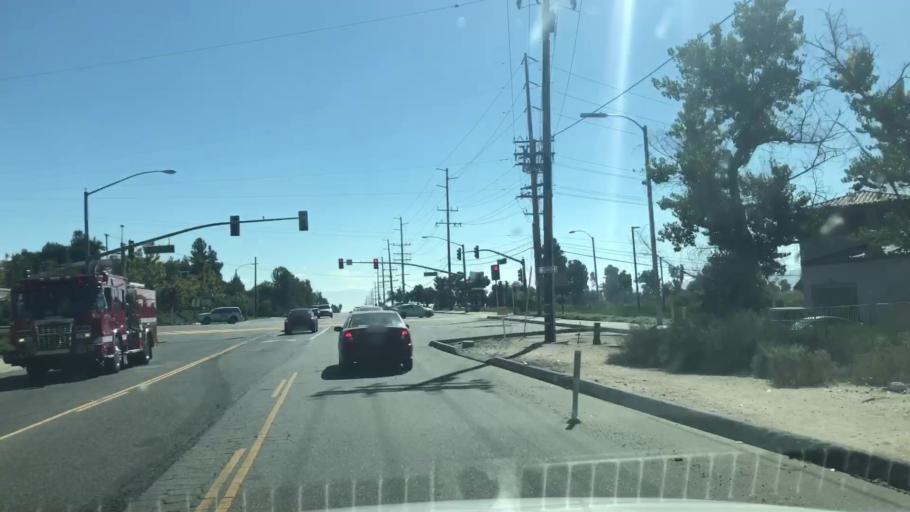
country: US
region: California
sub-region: Riverside County
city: Wildomar
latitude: 33.5897
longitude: -117.2528
